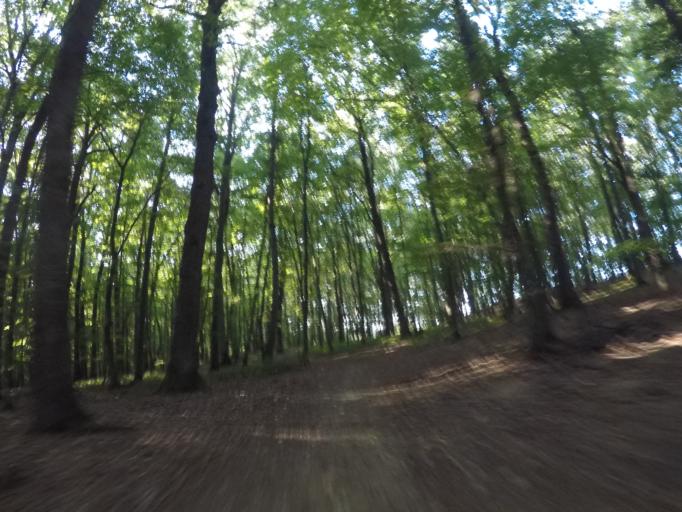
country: SK
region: Kosicky
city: Kosice
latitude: 48.7273
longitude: 21.1572
